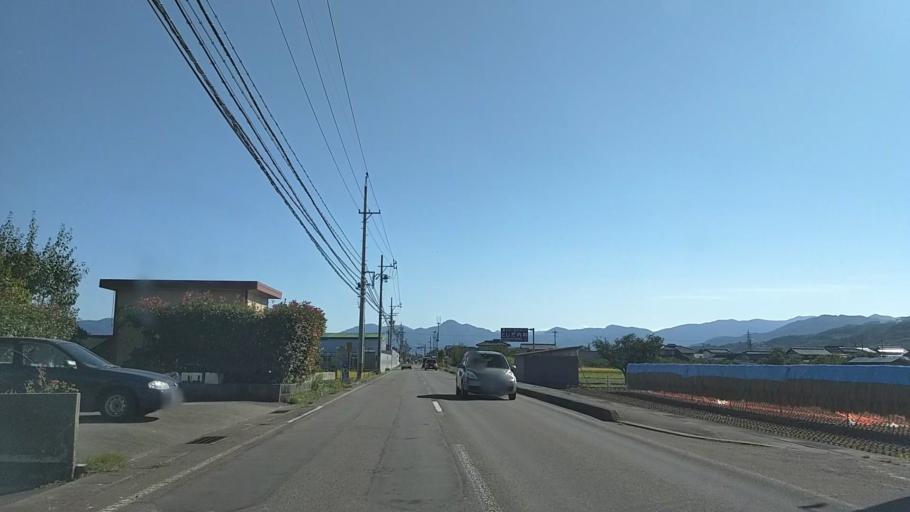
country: JP
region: Nagano
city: Nagano-shi
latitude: 36.6057
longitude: 138.1430
